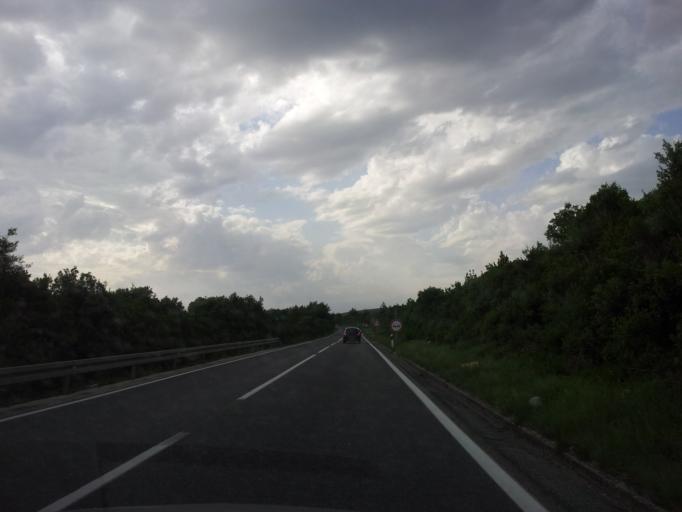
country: HR
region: Zadarska
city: Sukosan
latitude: 44.0171
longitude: 15.3589
